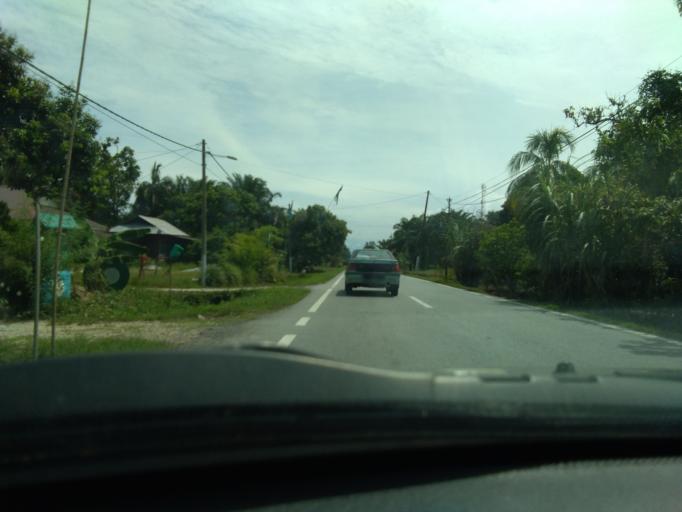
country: MY
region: Perak
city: Bagan Serai
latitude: 5.0334
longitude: 100.5641
